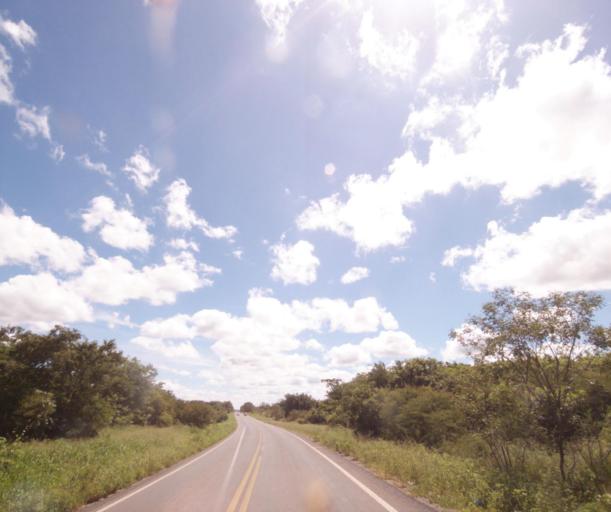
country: BR
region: Bahia
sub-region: Sao Felix Do Coribe
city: Santa Maria da Vitoria
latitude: -13.4065
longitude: -44.1572
